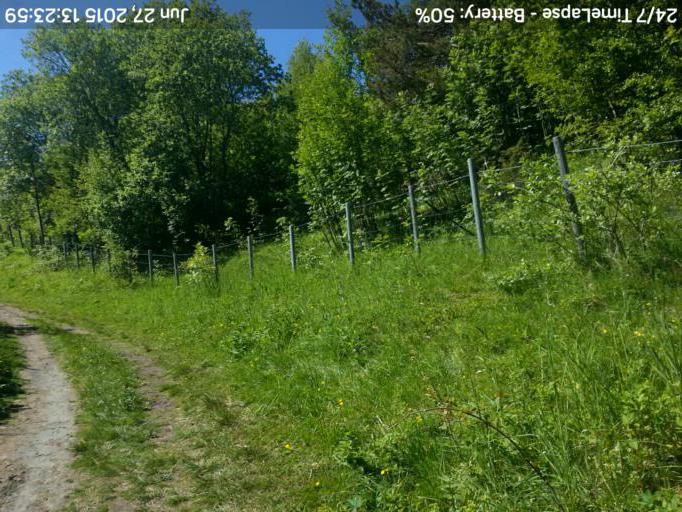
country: NO
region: Sor-Trondelag
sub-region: Trondheim
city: Trondheim
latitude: 63.3995
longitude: 10.3069
